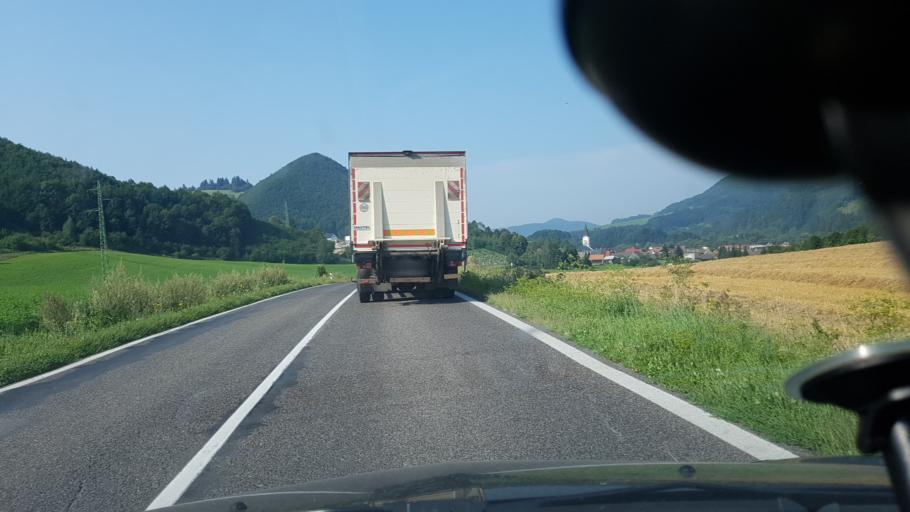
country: SK
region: Zilinsky
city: Tvrdosin
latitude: 49.2857
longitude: 19.4884
